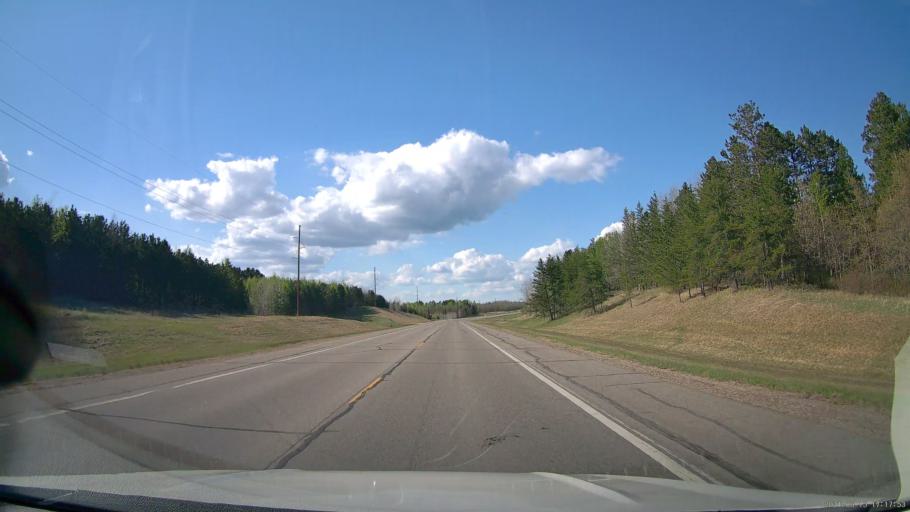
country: US
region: Minnesota
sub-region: Hubbard County
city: Park Rapids
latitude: 46.9522
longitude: -95.0177
